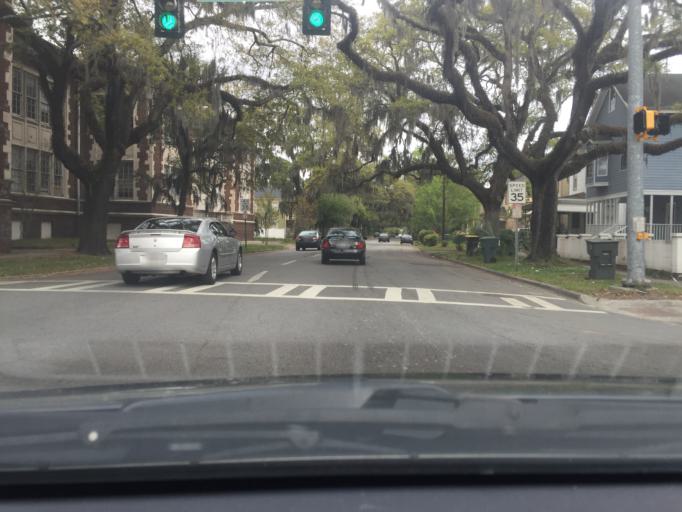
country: US
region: Georgia
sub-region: Chatham County
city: Savannah
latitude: 32.0580
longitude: -81.0820
